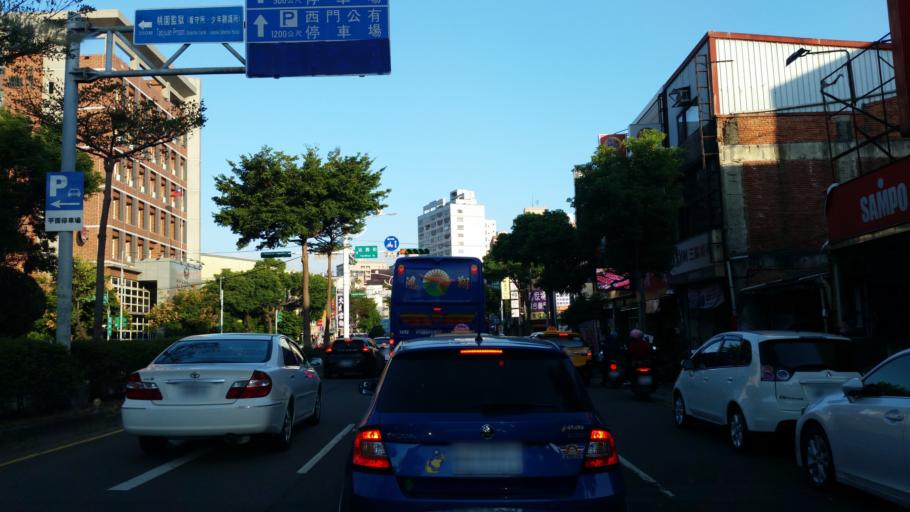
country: TW
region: Taiwan
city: Taoyuan City
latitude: 24.9912
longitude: 121.2931
